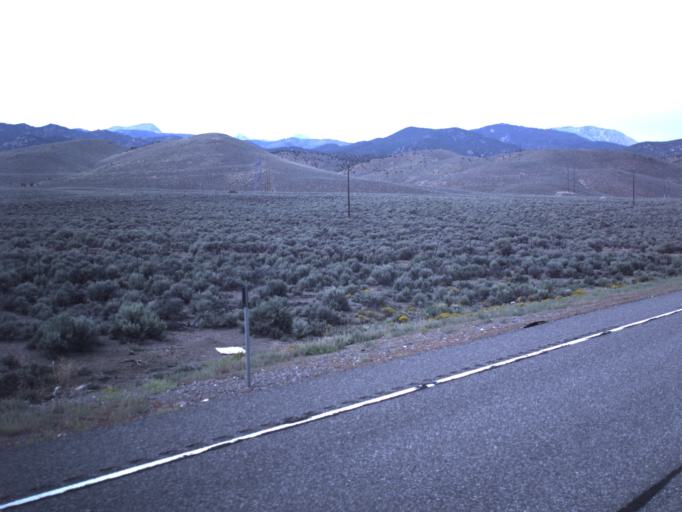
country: US
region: Utah
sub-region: Piute County
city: Junction
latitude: 38.2833
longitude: -112.2247
